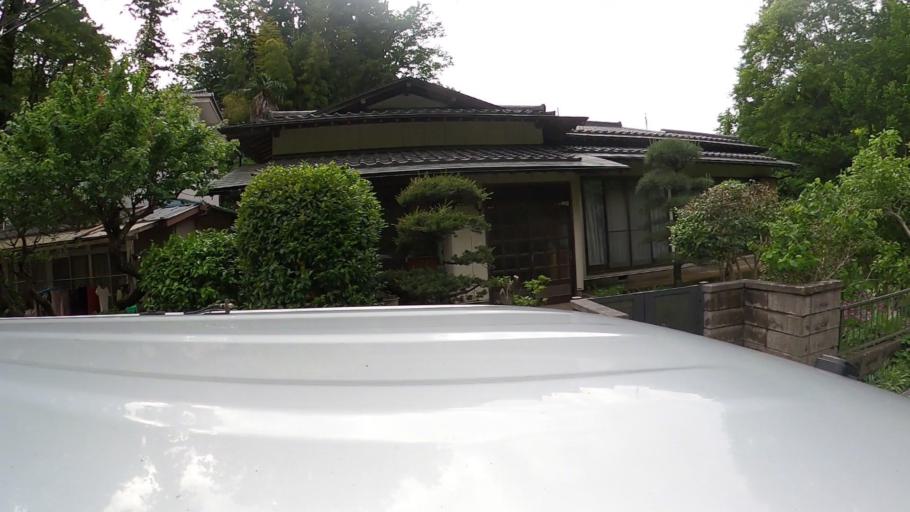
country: JP
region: Ibaraki
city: Ami
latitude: 35.9718
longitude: 140.2316
